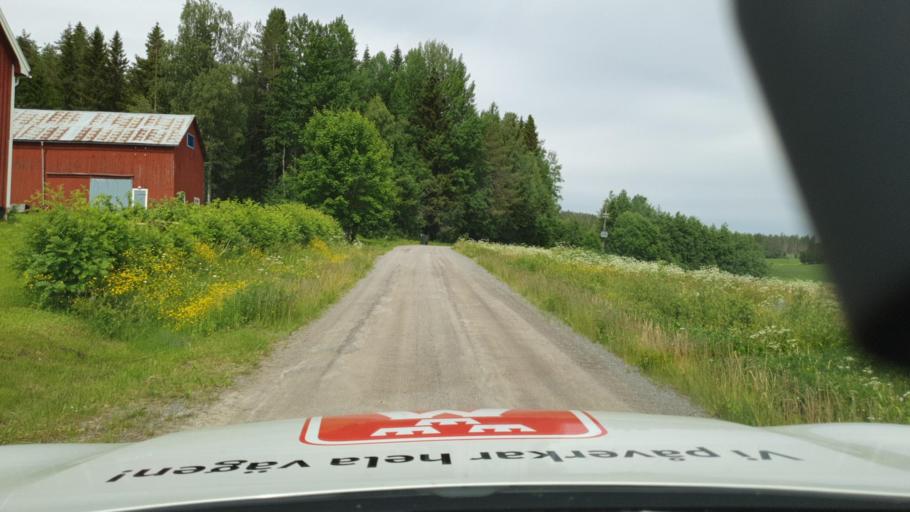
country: SE
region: Vaesterbotten
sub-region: Skelleftea Kommun
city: Burtraesk
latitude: 64.2716
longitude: 20.6067
